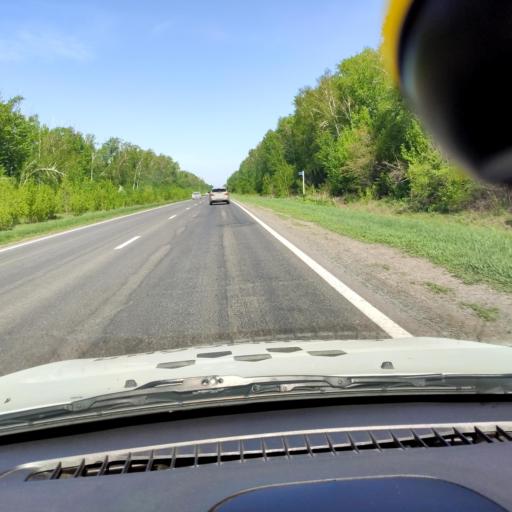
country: RU
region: Samara
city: Tol'yatti
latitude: 53.6085
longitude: 49.3176
